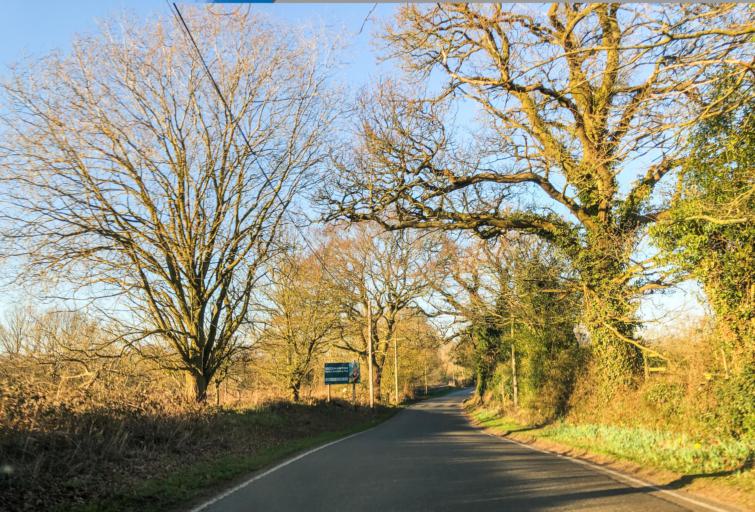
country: GB
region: England
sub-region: Warwickshire
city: Wroxall
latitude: 52.2962
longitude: -1.6587
